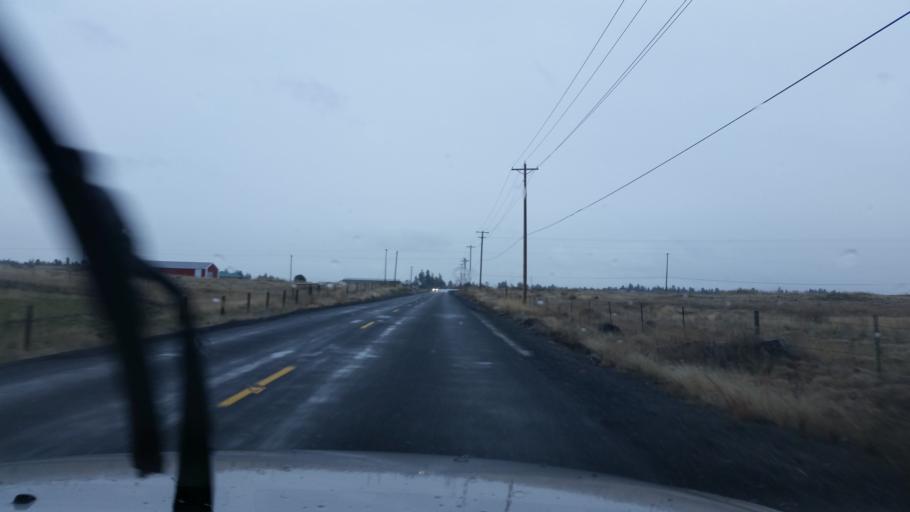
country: US
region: Washington
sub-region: Spokane County
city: Airway Heights
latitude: 47.6719
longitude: -117.5647
